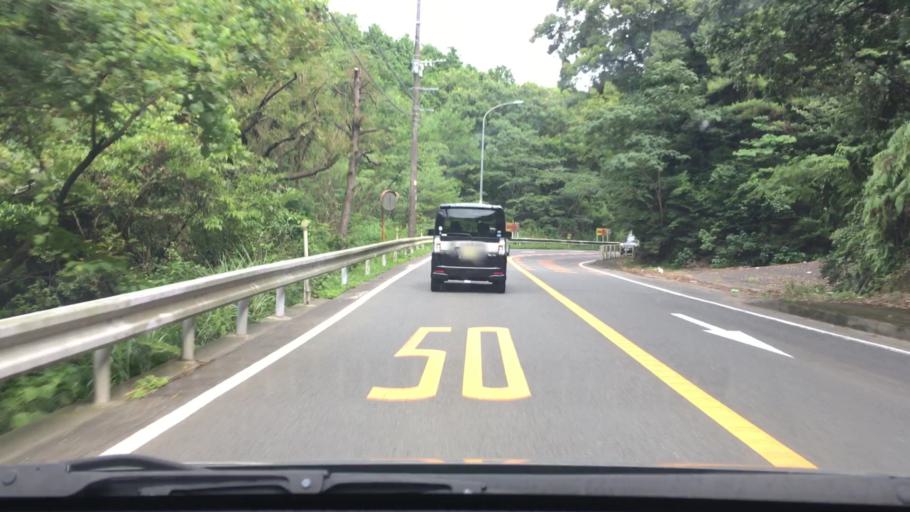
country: JP
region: Nagasaki
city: Togitsu
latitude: 32.9617
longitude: 129.7828
